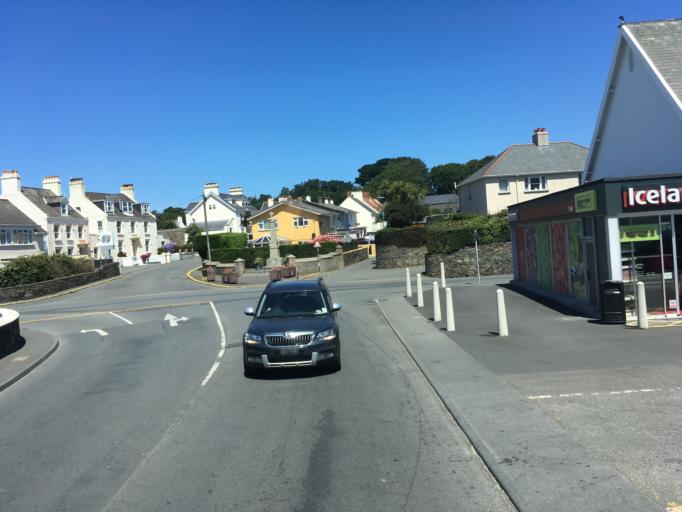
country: GG
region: St Peter Port
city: Saint Peter Port
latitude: 49.4864
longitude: -2.5191
